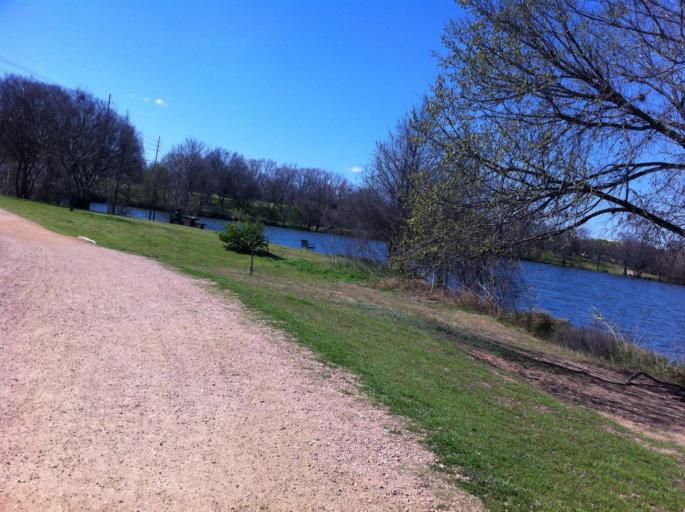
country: US
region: Texas
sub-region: Travis County
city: Austin
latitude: 30.2461
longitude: -97.7155
